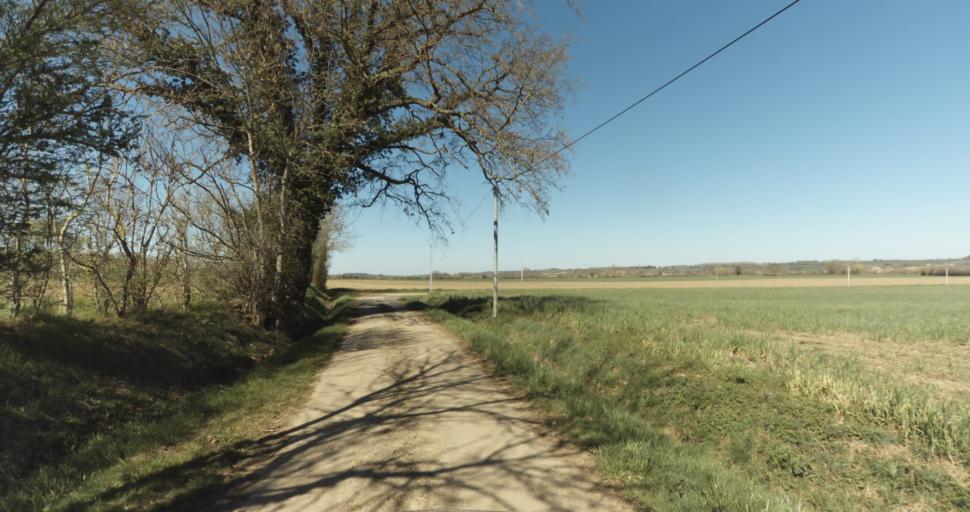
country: FR
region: Lower Normandy
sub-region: Departement du Calvados
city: Saint-Pierre-sur-Dives
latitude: 49.0219
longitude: 0.0136
